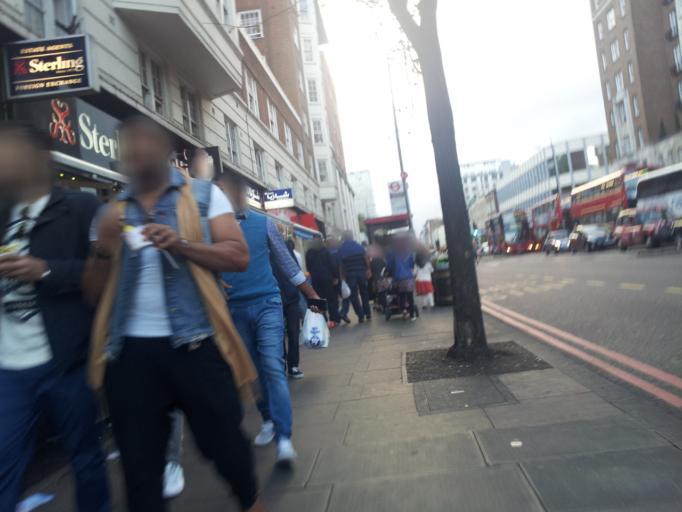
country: GB
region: England
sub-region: Greater London
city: Bayswater
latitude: 51.5162
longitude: -0.1649
